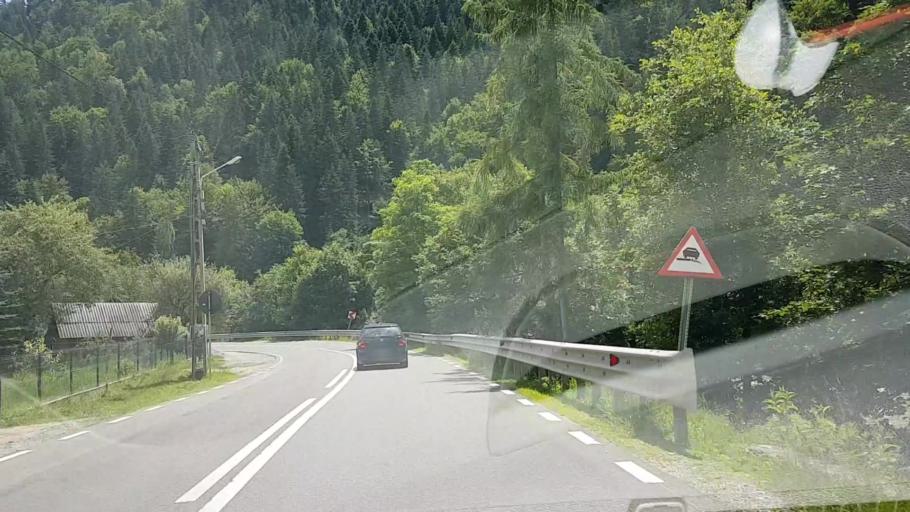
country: RO
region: Suceava
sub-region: Comuna Brosteni
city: Brosteni
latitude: 47.2572
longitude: 25.6699
